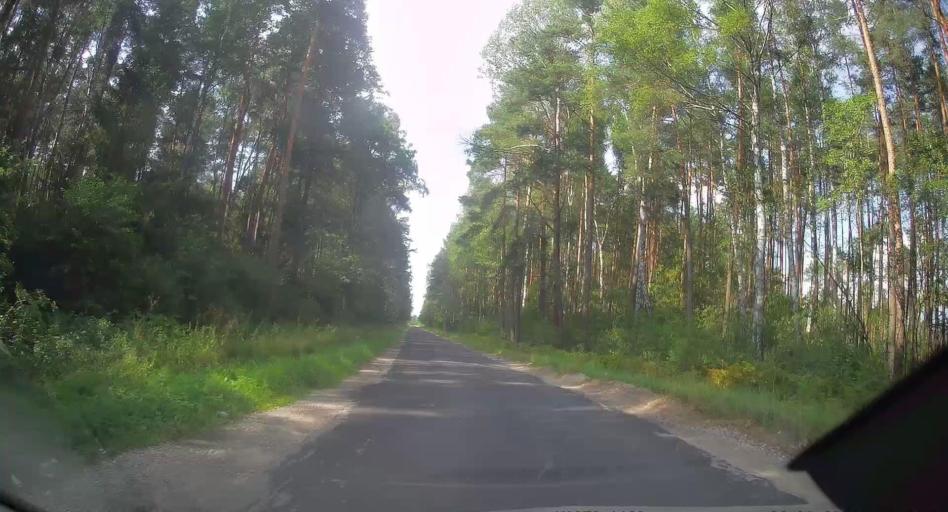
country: PL
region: Swietokrzyskie
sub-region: Powiat konecki
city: Radoszyce
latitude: 51.1031
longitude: 20.2659
